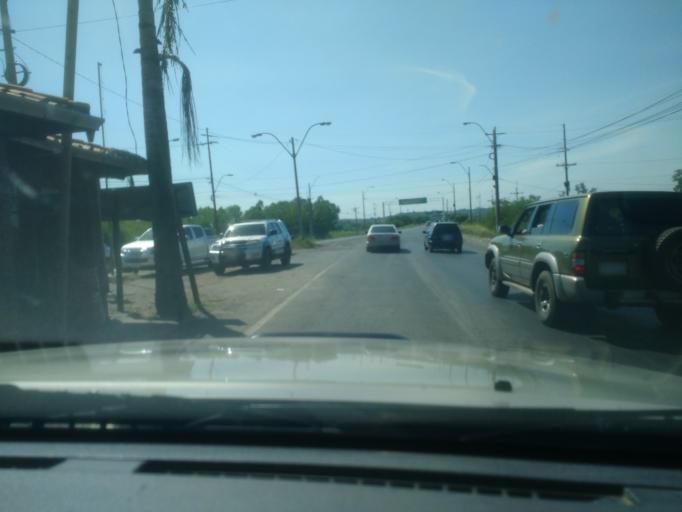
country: PY
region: Central
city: Colonia Mariano Roque Alonso
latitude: -25.1728
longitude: -57.5605
